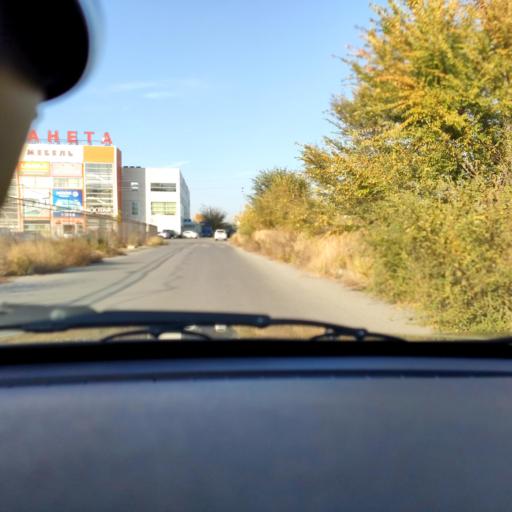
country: RU
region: Samara
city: Tol'yatti
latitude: 53.5512
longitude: 49.3251
